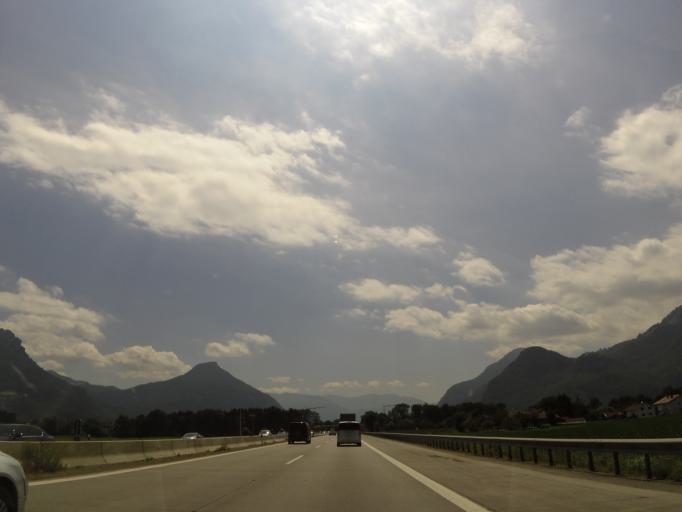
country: DE
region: Bavaria
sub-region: Upper Bavaria
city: Flintsbach
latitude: 47.7421
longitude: 12.1247
